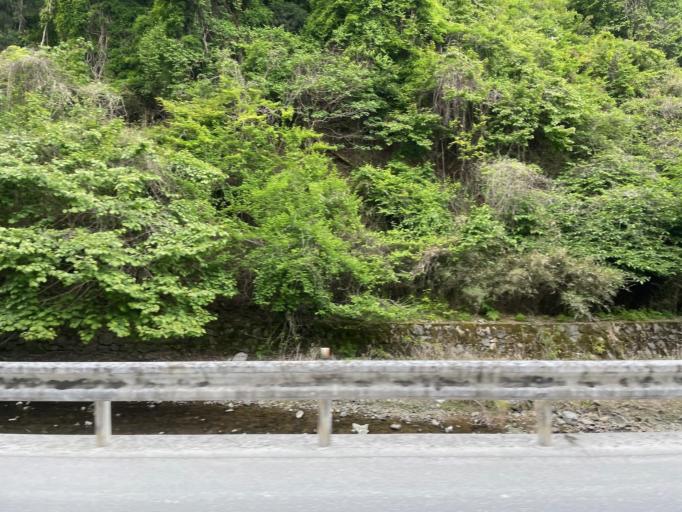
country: JP
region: Tochigi
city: Tanuma
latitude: 36.4565
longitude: 139.6075
